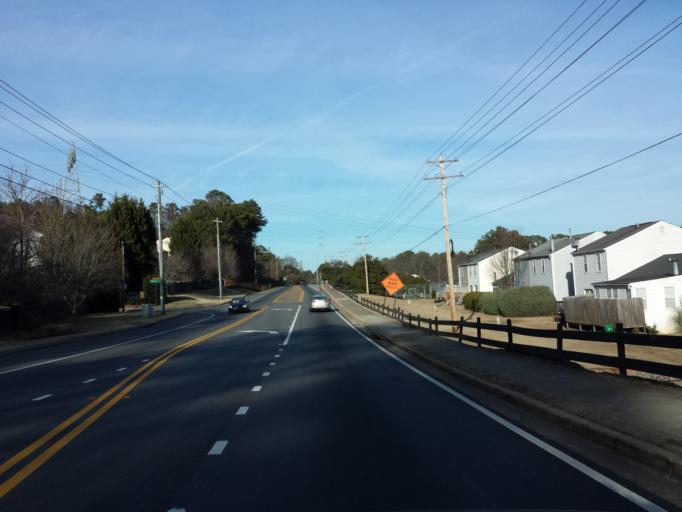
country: US
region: Georgia
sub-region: Cobb County
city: Marietta
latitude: 33.9949
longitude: -84.5488
